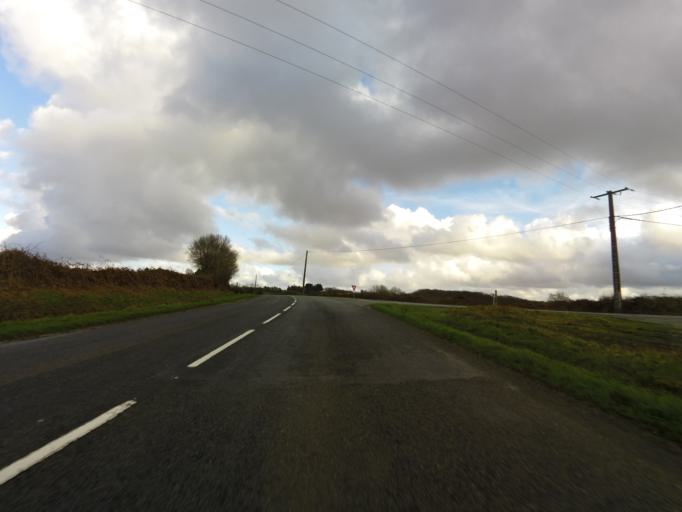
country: FR
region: Brittany
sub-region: Departement du Morbihan
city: Langonnet
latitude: 48.1433
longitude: -3.5147
